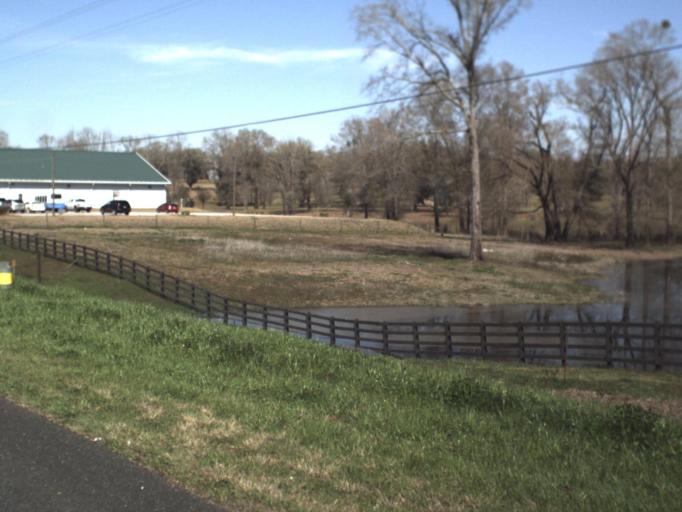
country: US
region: Florida
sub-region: Jackson County
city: Marianna
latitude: 30.8784
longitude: -85.3634
